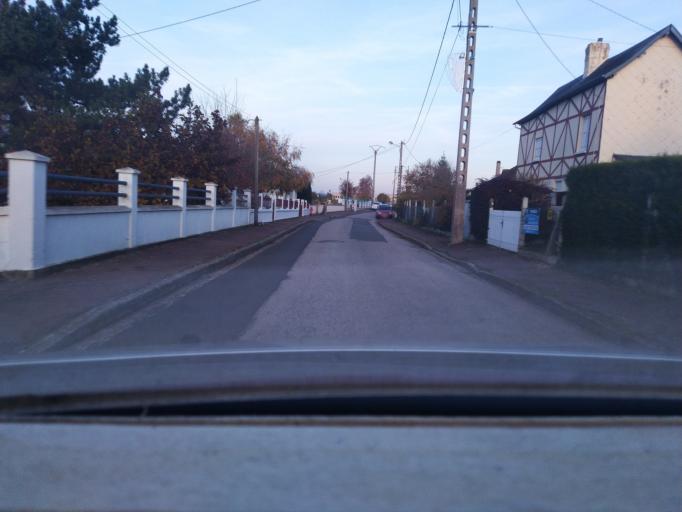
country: FR
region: Haute-Normandie
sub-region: Departement de la Seine-Maritime
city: Yainville
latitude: 49.4588
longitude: 0.8344
